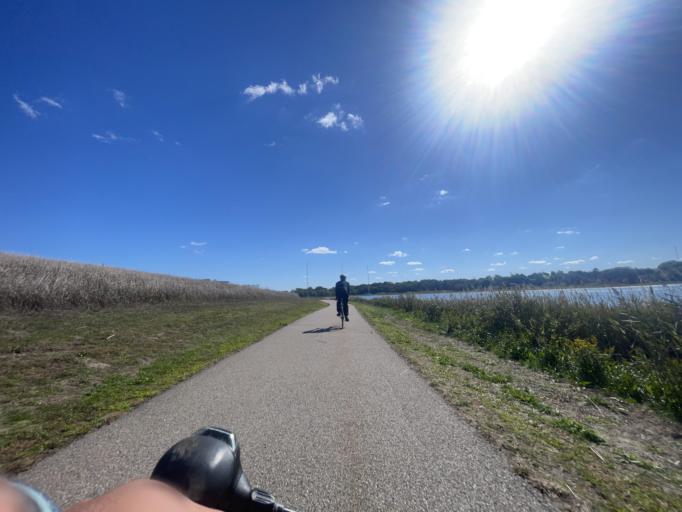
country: US
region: Massachusetts
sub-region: Norfolk County
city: Milton
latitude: 42.2776
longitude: -71.0464
